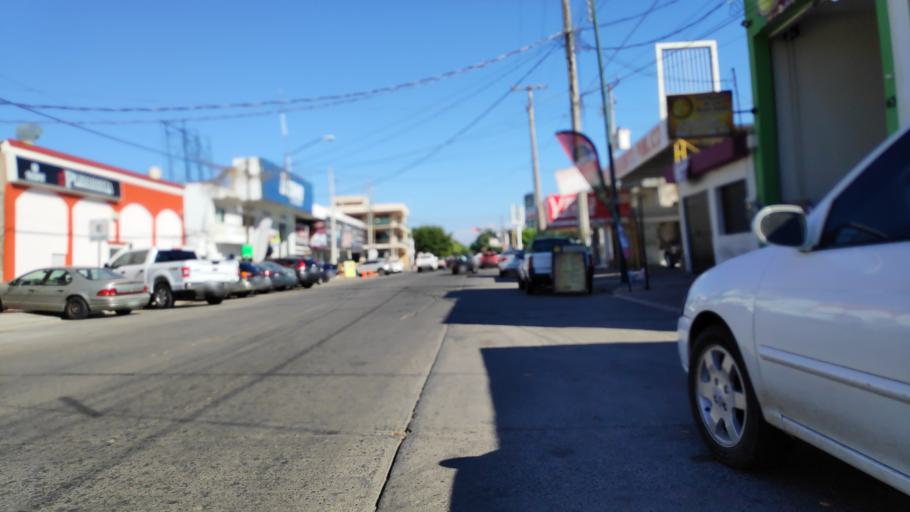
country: MX
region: Sinaloa
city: Culiacan
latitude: 24.8001
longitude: -107.3950
